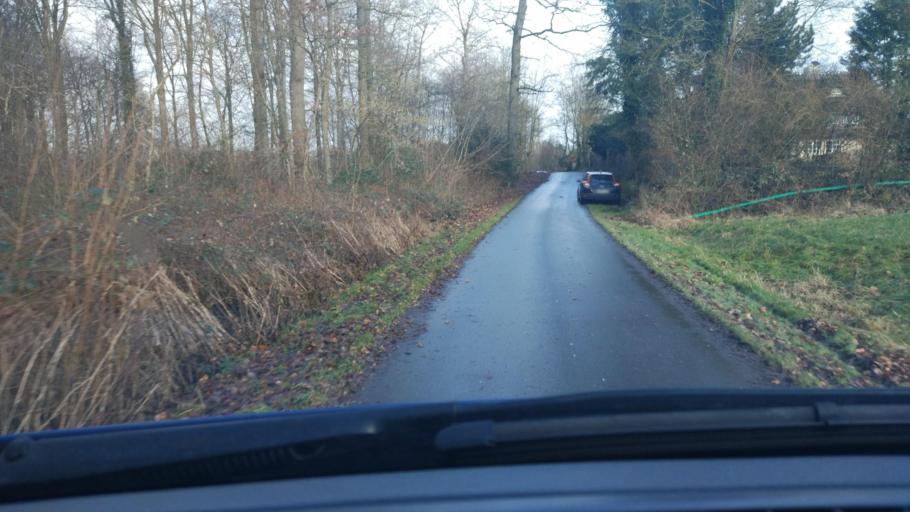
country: DE
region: Schleswig-Holstein
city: Taarstedt
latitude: 54.5557
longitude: 9.6833
